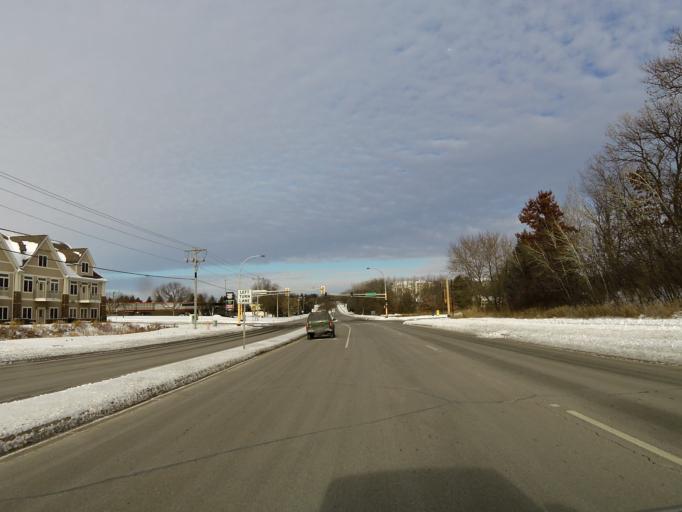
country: US
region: Minnesota
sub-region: Dakota County
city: Burnsville
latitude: 44.7362
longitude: -93.2986
